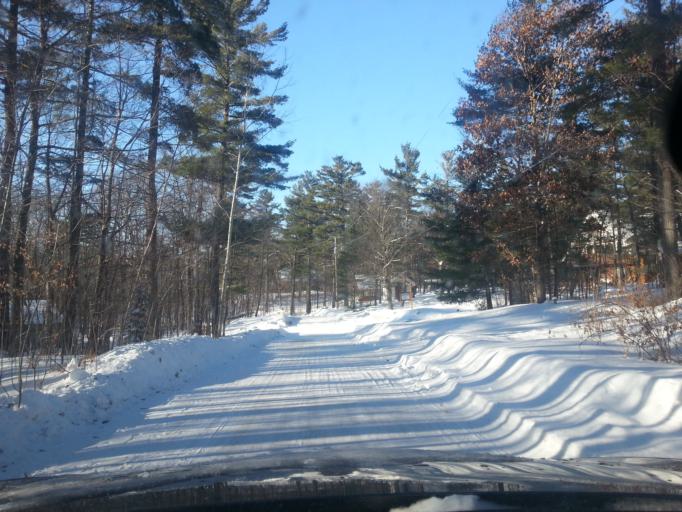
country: CA
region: Ontario
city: Arnprior
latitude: 45.3248
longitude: -76.3260
